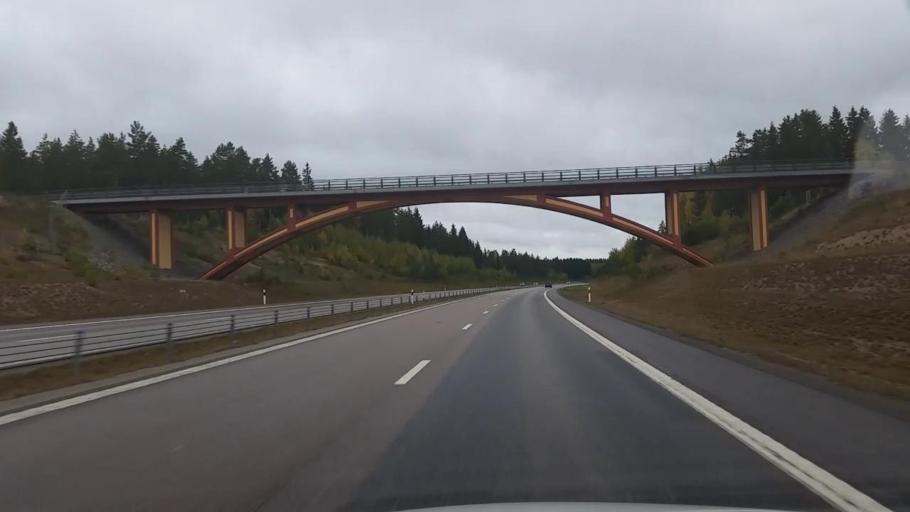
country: SE
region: Uppsala
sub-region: Osthammars Kommun
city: Bjorklinge
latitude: 60.1200
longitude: 17.5476
